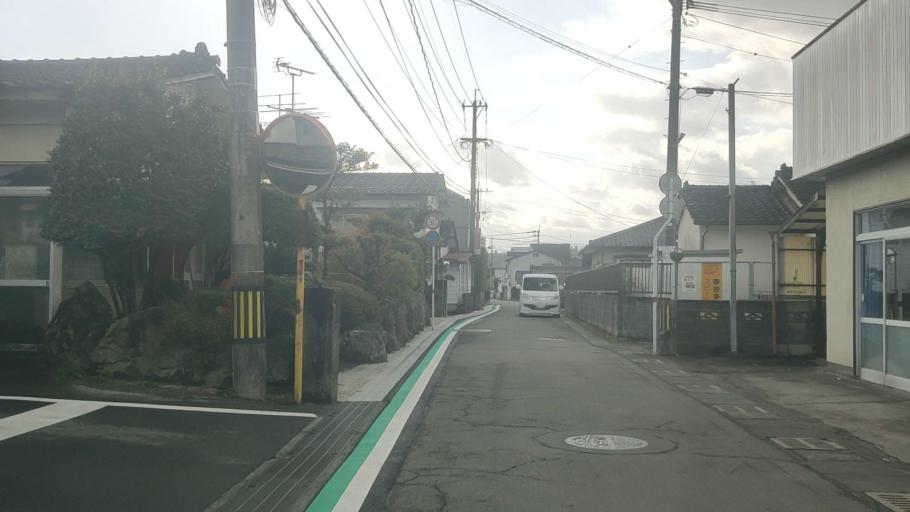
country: JP
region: Kumamoto
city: Hitoyoshi
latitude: 32.2209
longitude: 130.7715
